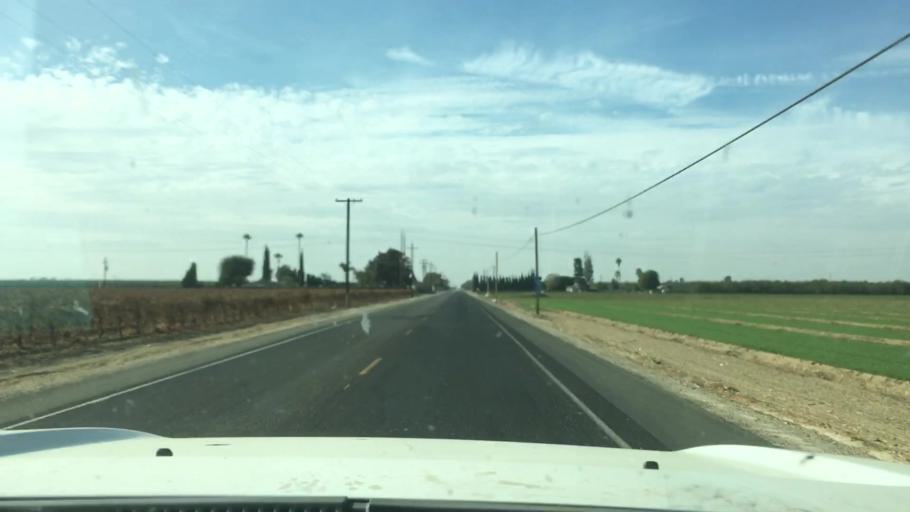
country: US
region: California
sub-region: Kern County
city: Shafter
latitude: 35.4999
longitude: -119.3153
